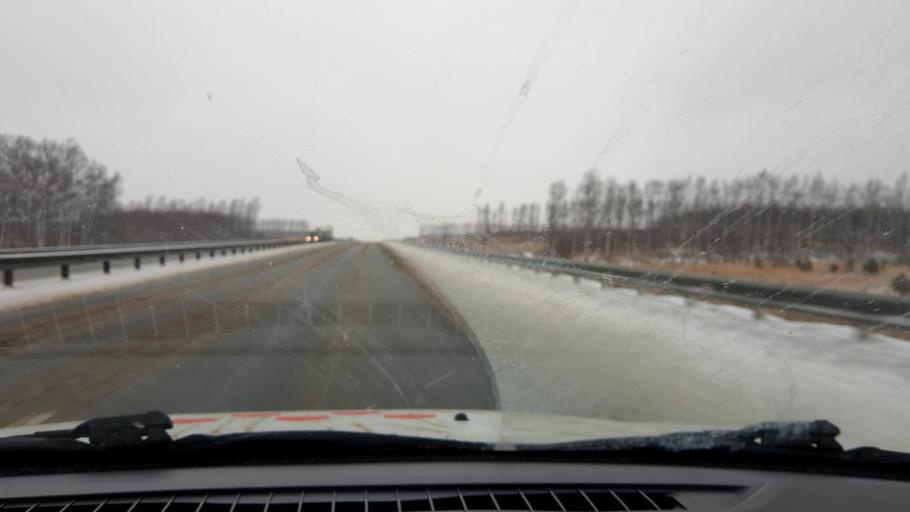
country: RU
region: Nizjnij Novgorod
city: Afonino
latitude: 56.1020
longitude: 44.0176
